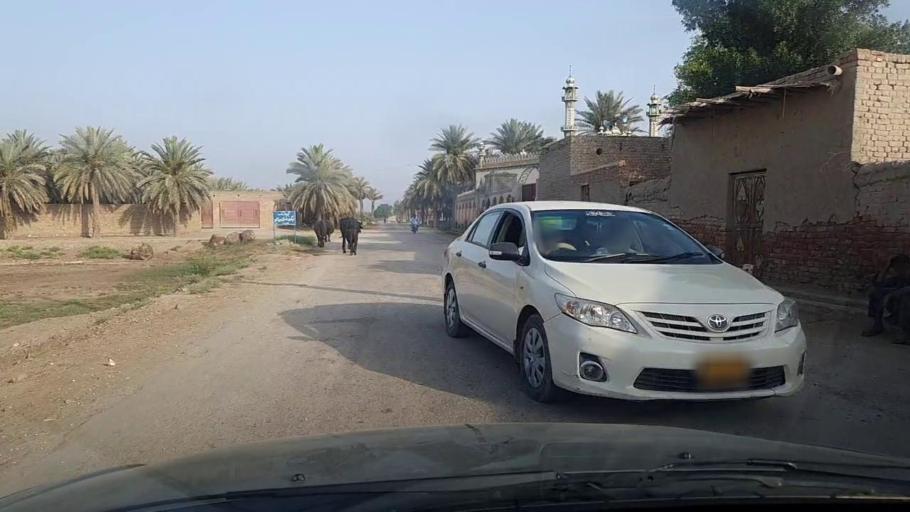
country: PK
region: Sindh
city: Khairpur
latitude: 27.5435
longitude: 68.7043
